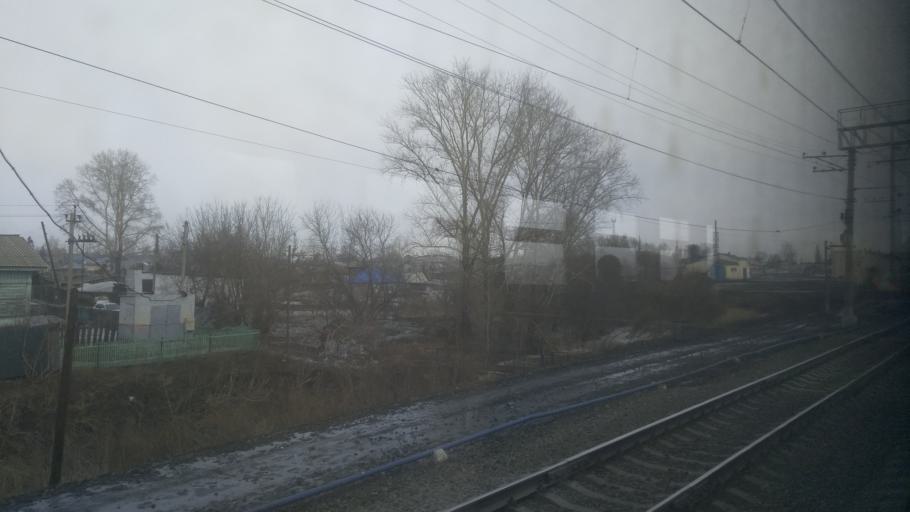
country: RU
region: Kemerovo
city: Yurga
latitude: 55.7112
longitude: 84.8343
